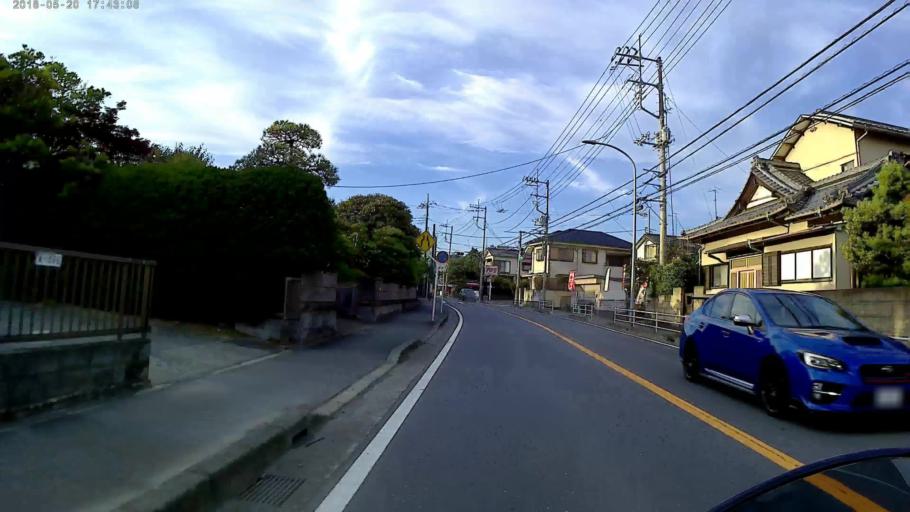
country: JP
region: Kanagawa
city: Ninomiya
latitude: 35.3115
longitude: 139.2779
